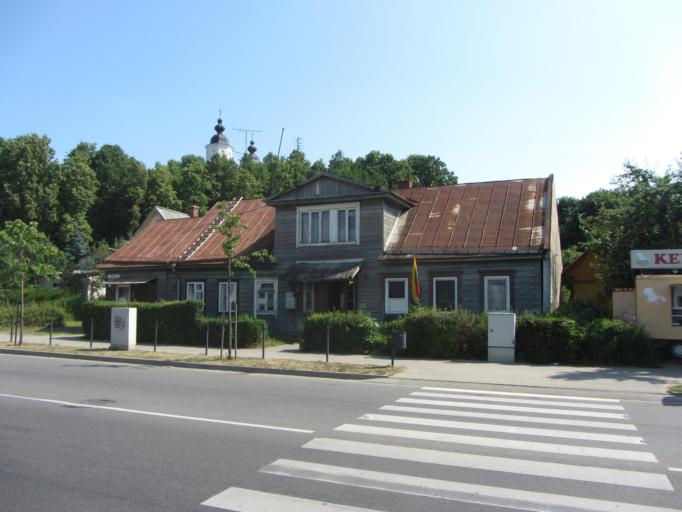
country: LT
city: Zarasai
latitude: 55.7295
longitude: 26.2441
